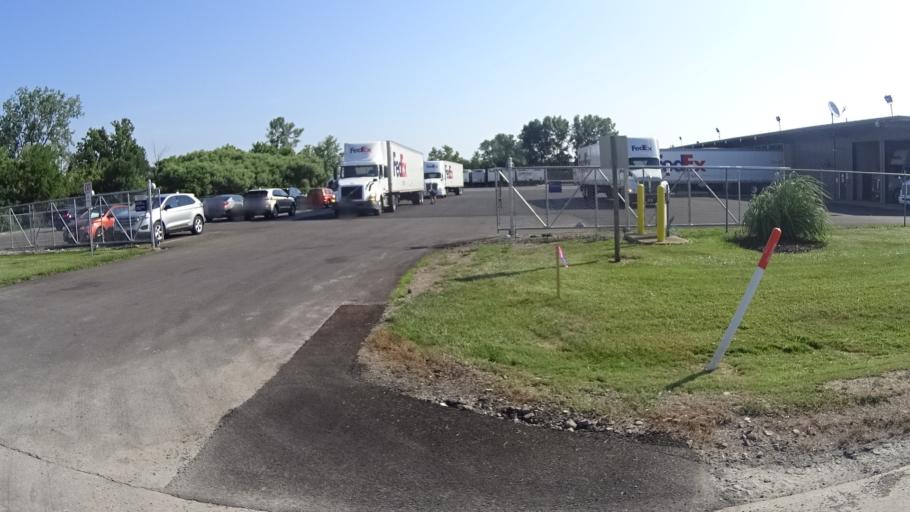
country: US
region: Ohio
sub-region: Erie County
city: Huron
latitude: 41.3999
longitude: -82.5842
